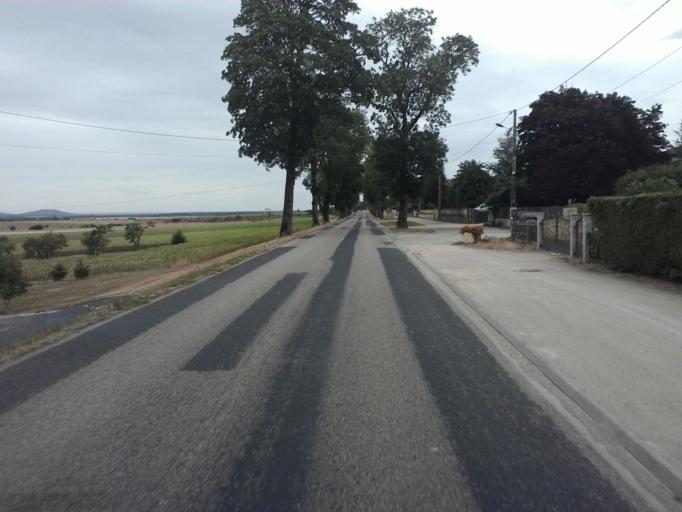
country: FR
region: Lorraine
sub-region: Departement de Meurthe-et-Moselle
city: Colombey-les-Belles
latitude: 48.5329
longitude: 5.8990
